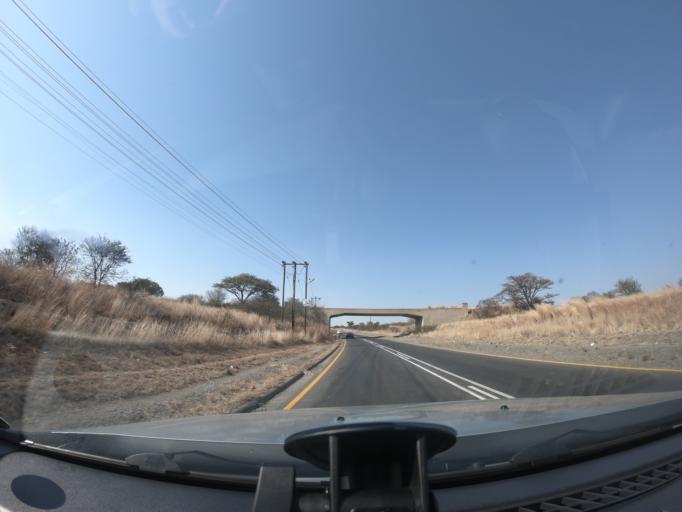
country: ZA
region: KwaZulu-Natal
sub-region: uThukela District Municipality
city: Ladysmith
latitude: -28.5430
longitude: 29.8075
